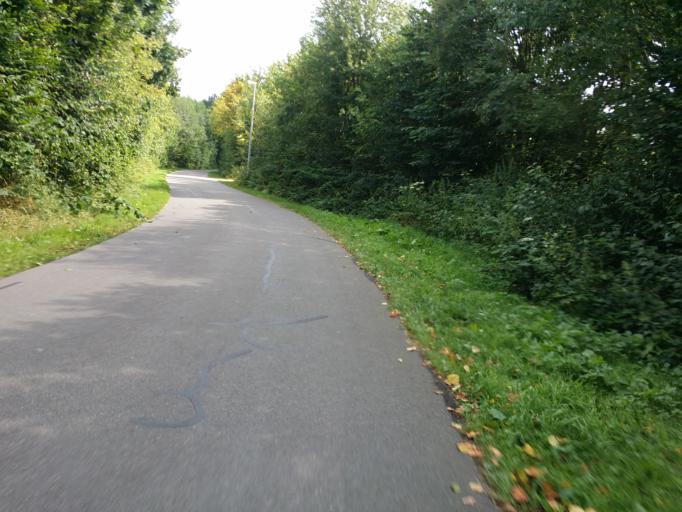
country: DE
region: Schleswig-Holstein
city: Mehlbek
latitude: 54.0035
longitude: 9.4300
